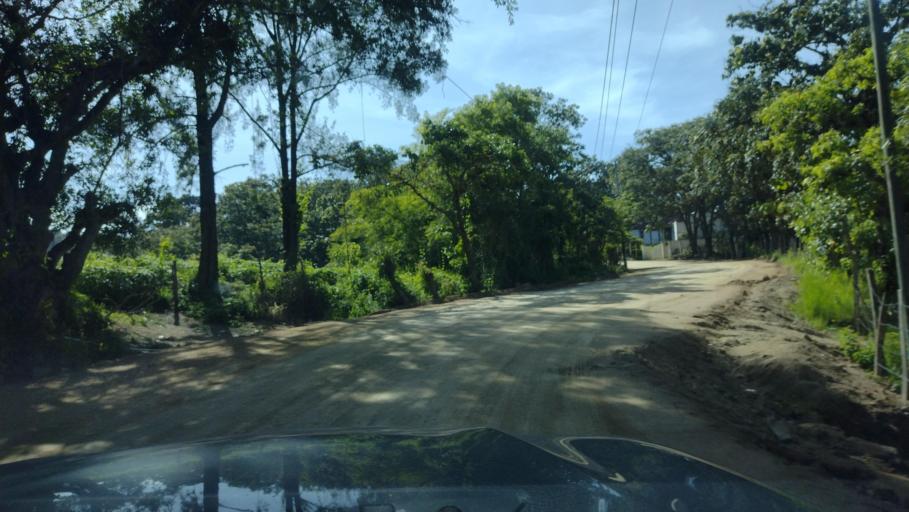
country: GT
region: Guatemala
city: Chinautla
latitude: 14.7606
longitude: -90.5231
